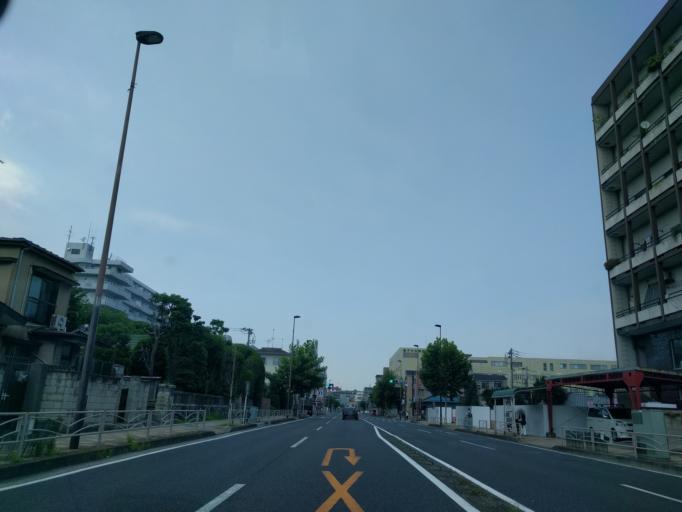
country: JP
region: Kanagawa
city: Yokohama
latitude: 35.4058
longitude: 139.6203
